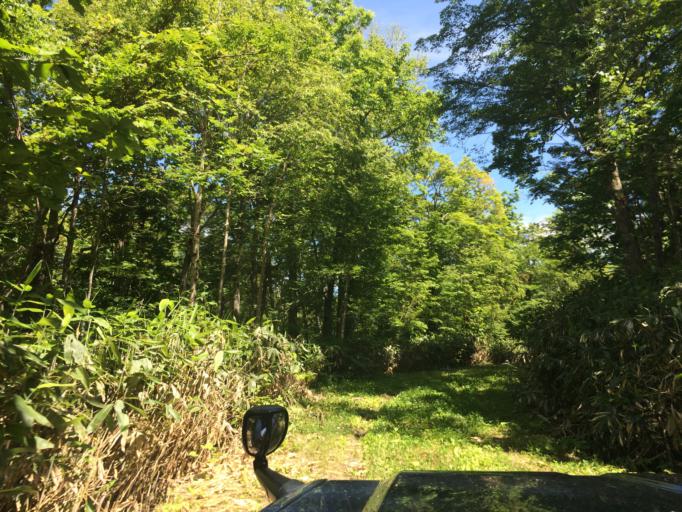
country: JP
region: Hokkaido
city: Niseko Town
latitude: 42.8568
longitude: 140.8200
